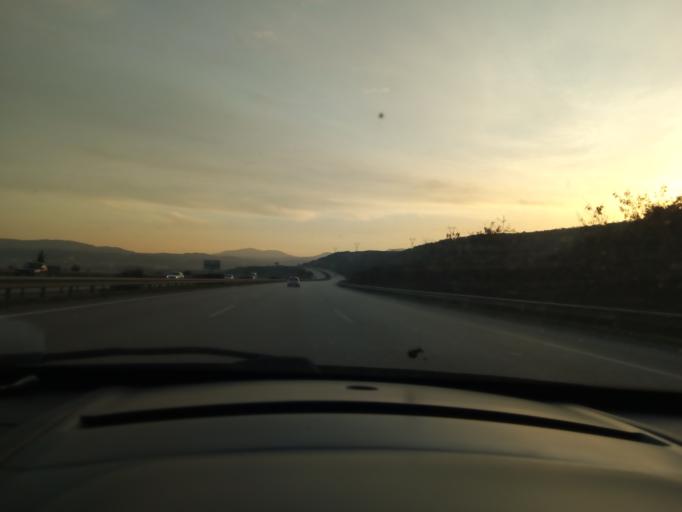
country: TR
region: Bursa
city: Niluefer
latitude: 40.2732
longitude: 28.9667
